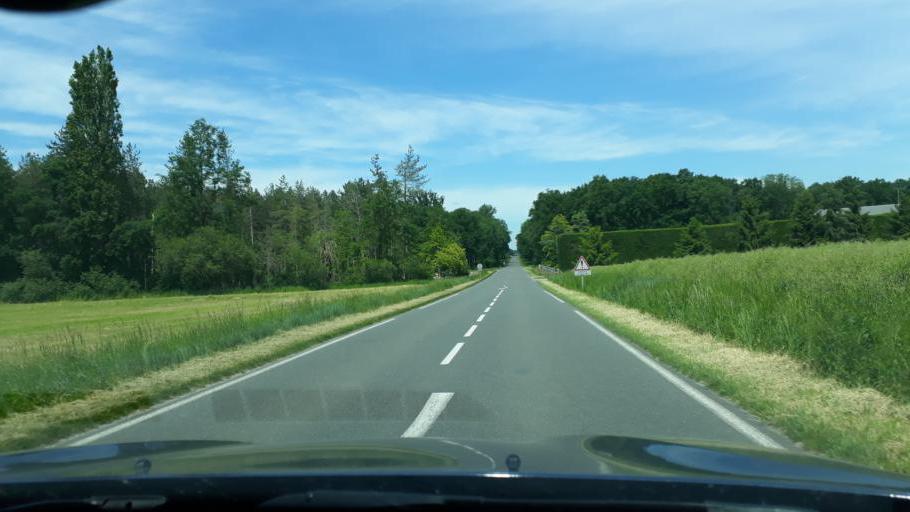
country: FR
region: Centre
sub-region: Departement du Loiret
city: Boiscommun
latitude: 48.0327
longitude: 2.3101
